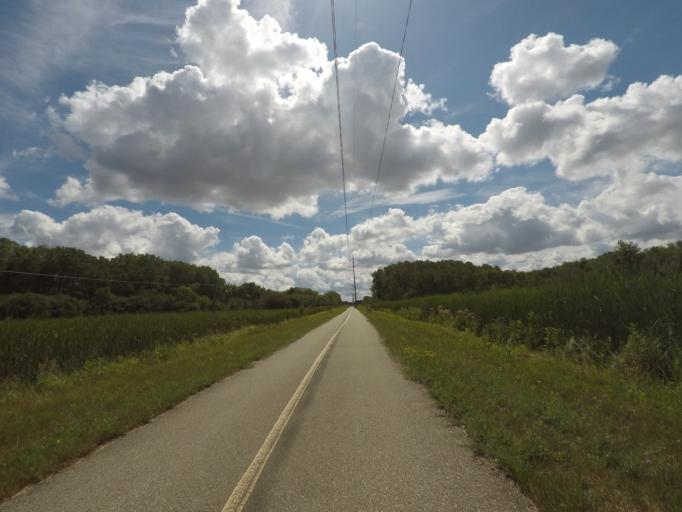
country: US
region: Wisconsin
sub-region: Waukesha County
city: Pewaukee
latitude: 43.0586
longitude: -88.2951
